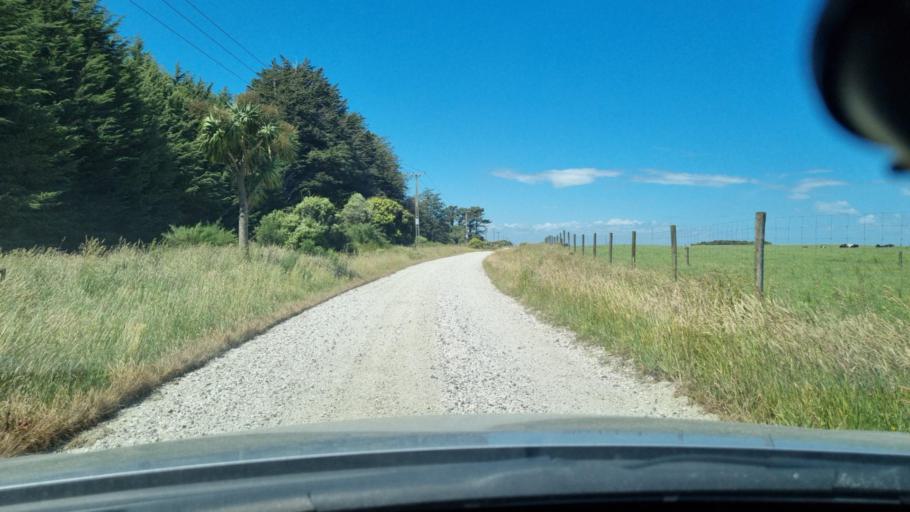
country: NZ
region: Southland
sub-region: Invercargill City
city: Invercargill
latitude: -46.4425
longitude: 168.4227
